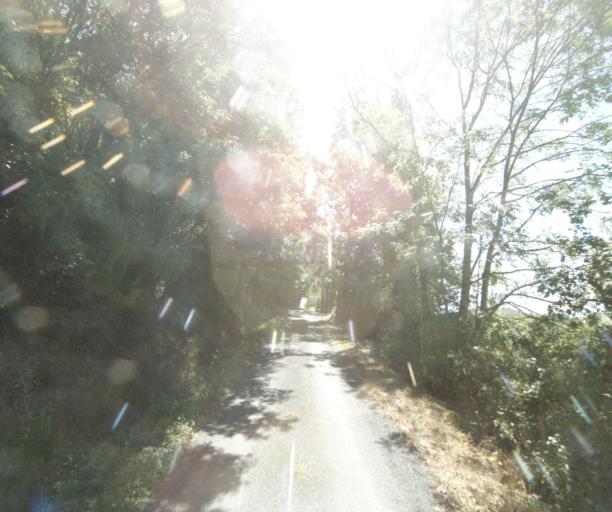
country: FR
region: Rhone-Alpes
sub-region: Departement du Rhone
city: Bessenay
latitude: 45.7947
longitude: 4.5271
